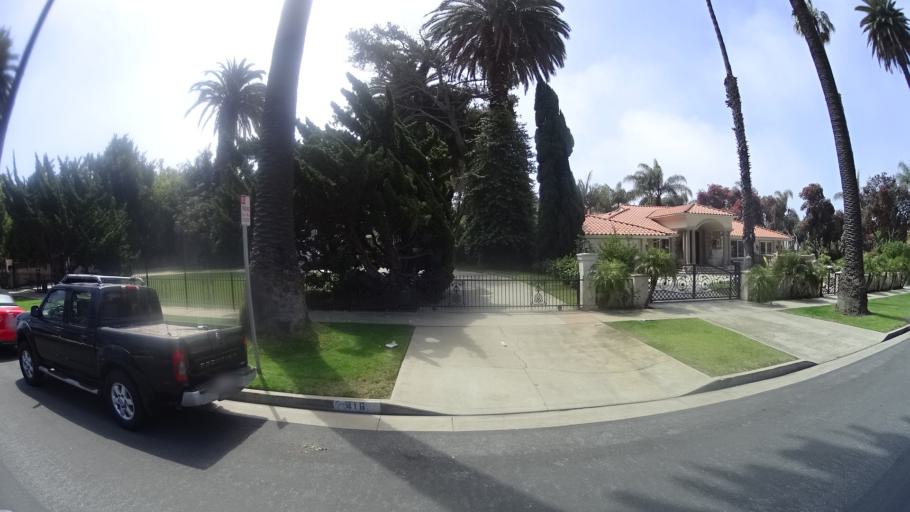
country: US
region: California
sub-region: Los Angeles County
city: Santa Monica
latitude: 34.0275
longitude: -118.5078
